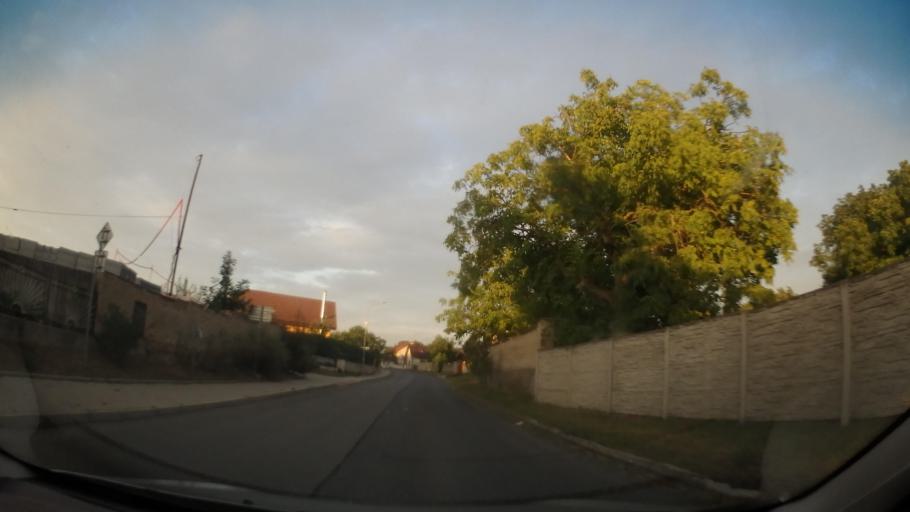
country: CZ
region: Central Bohemia
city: Milovice
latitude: 50.2233
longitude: 14.8933
